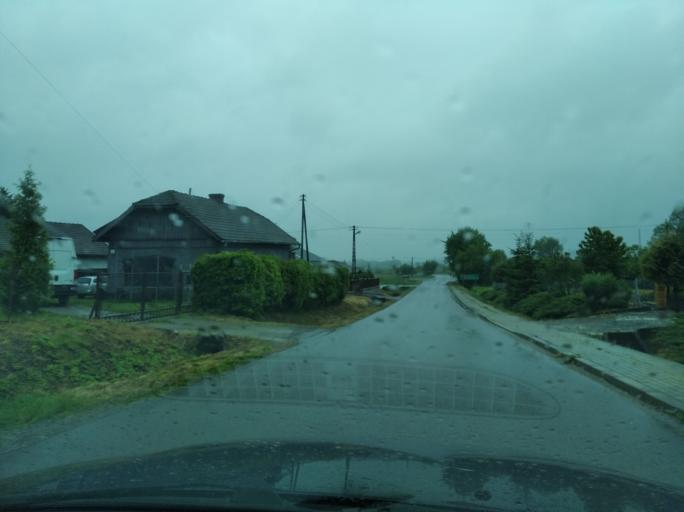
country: PL
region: Subcarpathian Voivodeship
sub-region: Powiat jasielski
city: Tarnowiec
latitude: 49.7618
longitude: 21.5398
